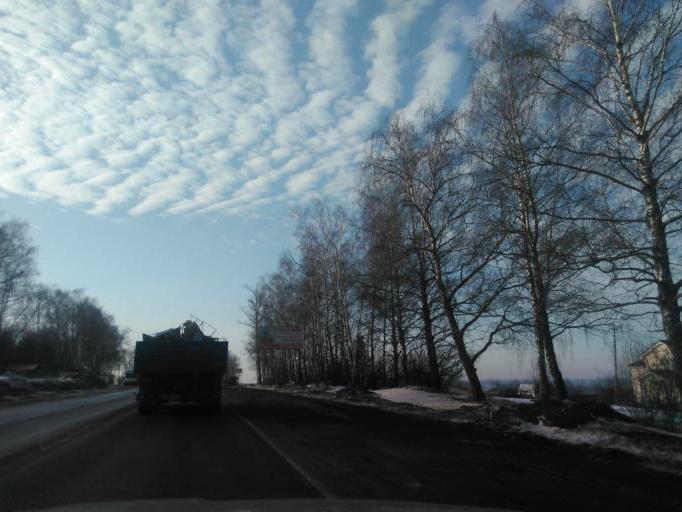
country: RU
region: Moskovskaya
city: Snegiri
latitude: 55.8755
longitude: 36.9429
